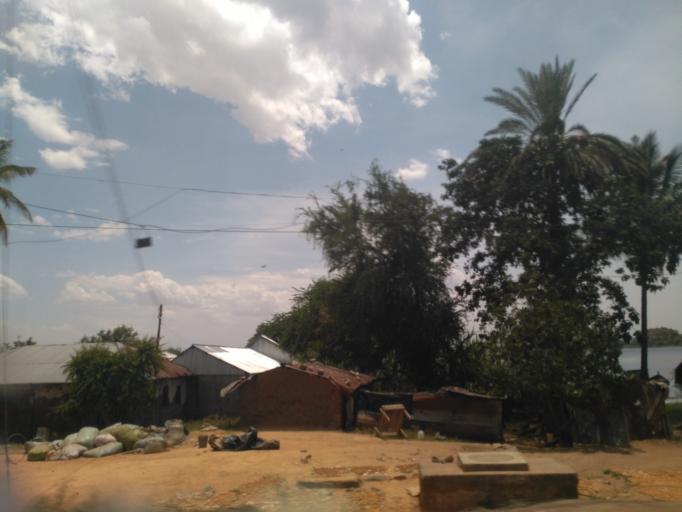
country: TZ
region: Mwanza
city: Mwanza
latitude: -2.5489
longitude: 32.9061
